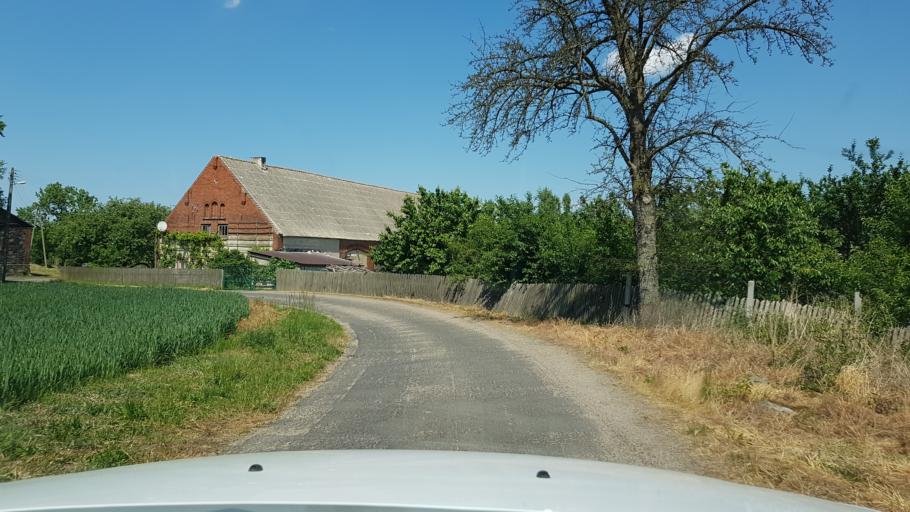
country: PL
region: West Pomeranian Voivodeship
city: Trzcinsko Zdroj
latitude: 52.9315
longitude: 14.5819
